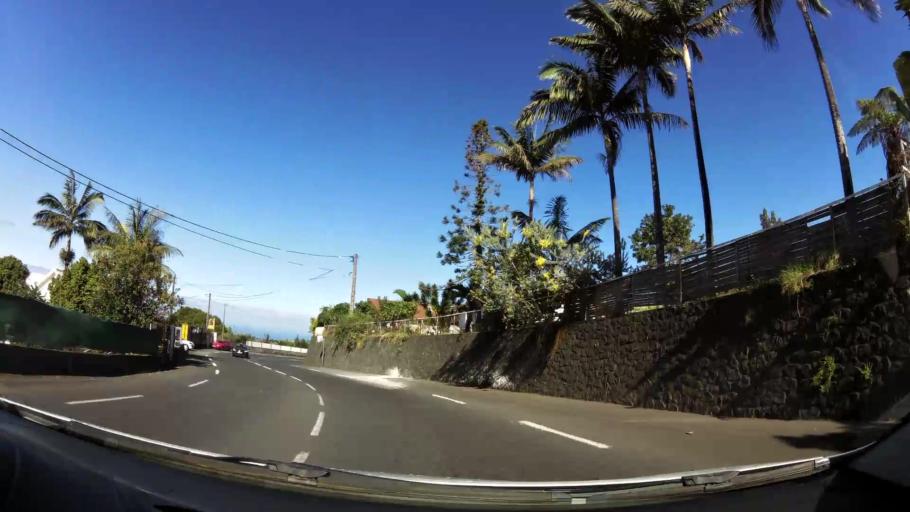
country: RE
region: Reunion
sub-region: Reunion
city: Le Tampon
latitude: -21.2444
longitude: 55.5262
